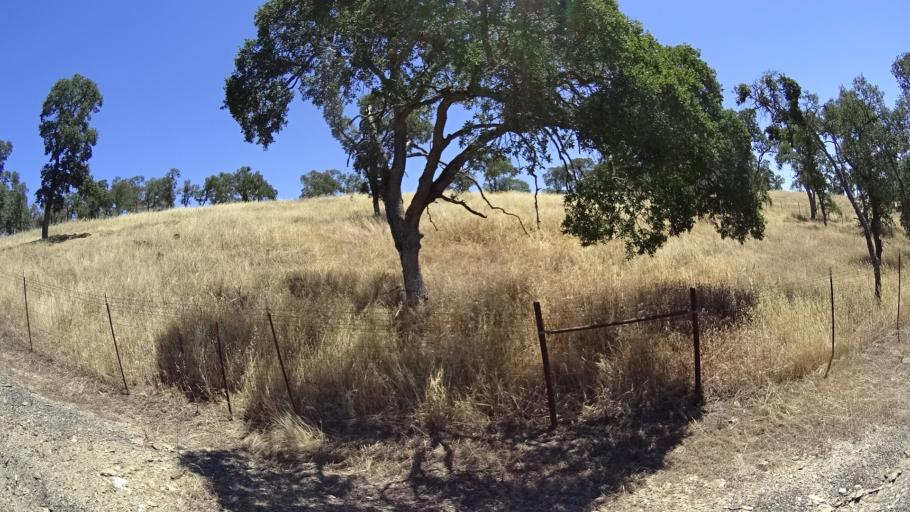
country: US
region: California
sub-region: Calaveras County
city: Copperopolis
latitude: 37.9919
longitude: -120.7008
